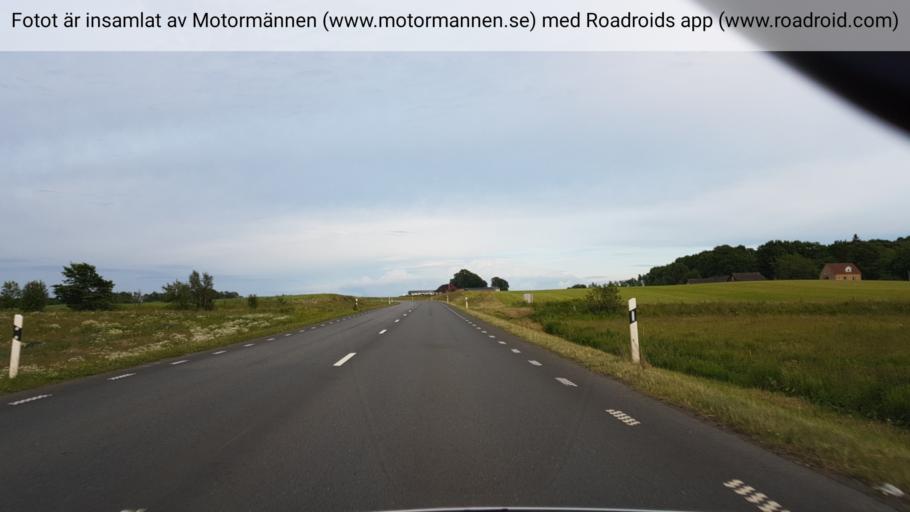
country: SE
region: Vaestra Goetaland
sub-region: Falkopings Kommun
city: Falkoeping
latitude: 58.1821
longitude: 13.5746
